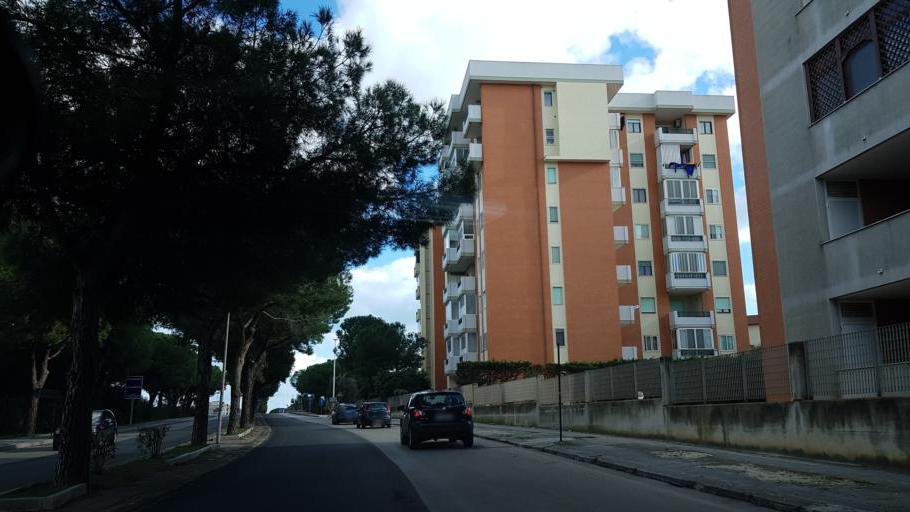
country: IT
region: Apulia
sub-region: Provincia di Brindisi
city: Brindisi
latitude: 40.6214
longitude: 17.9221
